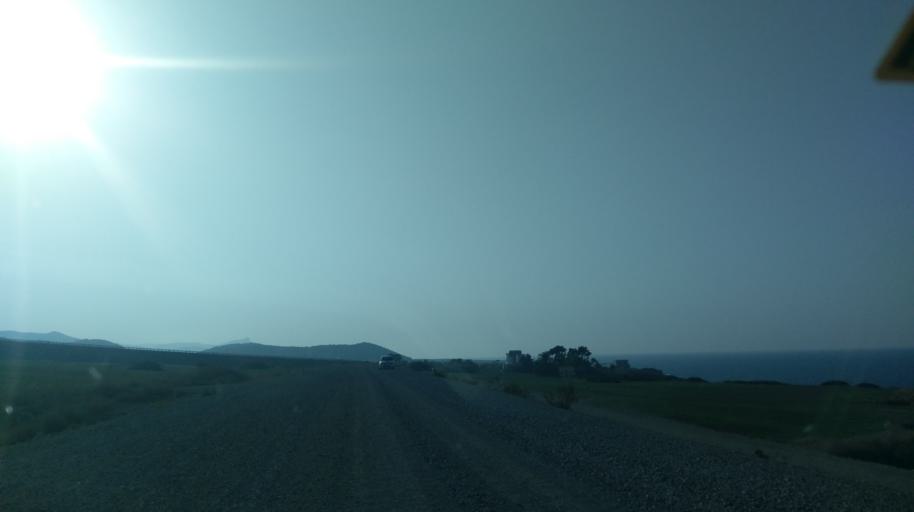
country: CY
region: Ammochostos
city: Leonarisso
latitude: 35.4955
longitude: 34.1001
